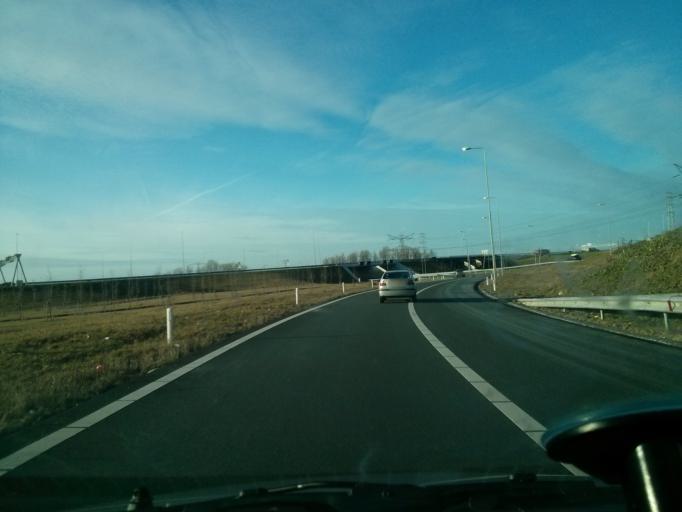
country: NL
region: Gelderland
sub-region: Gemeente Overbetuwe
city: Herveld
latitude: 51.9073
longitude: 5.7711
